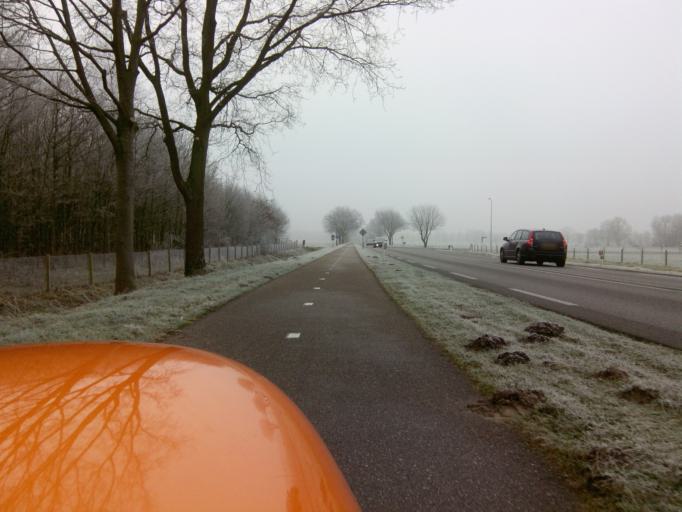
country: NL
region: Gelderland
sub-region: Gemeente Barneveld
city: Garderen
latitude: 52.2797
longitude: 5.7116
